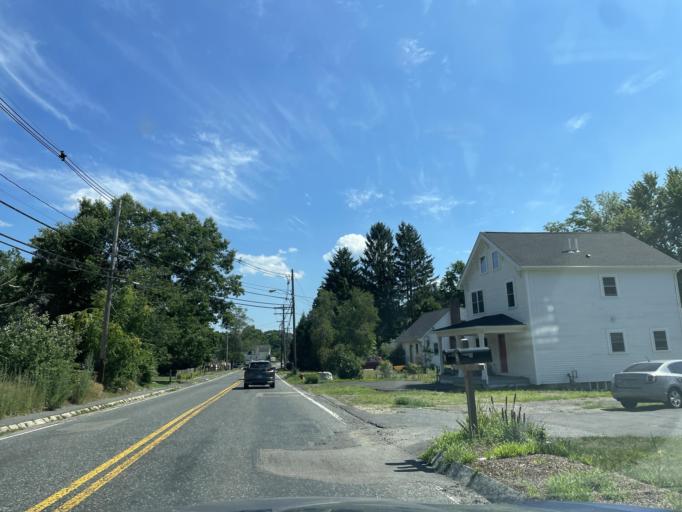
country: US
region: Massachusetts
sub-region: Middlesex County
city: Holliston
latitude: 42.2176
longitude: -71.4264
